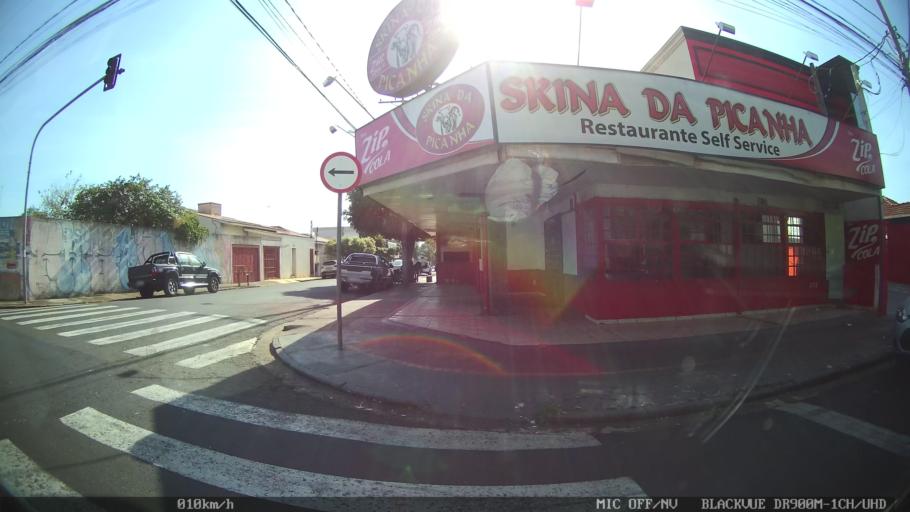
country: BR
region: Sao Paulo
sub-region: Sao Jose Do Rio Preto
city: Sao Jose do Rio Preto
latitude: -20.8035
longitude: -49.3901
